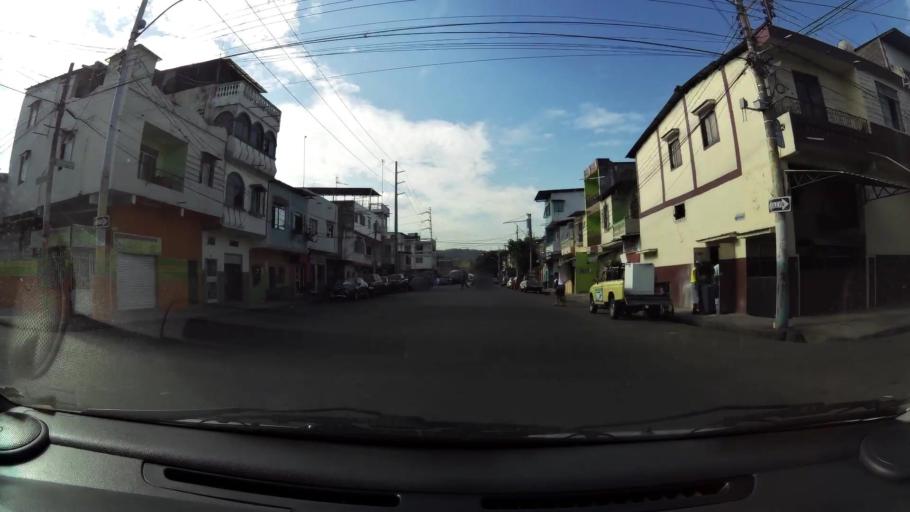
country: EC
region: Guayas
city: Guayaquil
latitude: -2.1951
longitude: -79.9246
